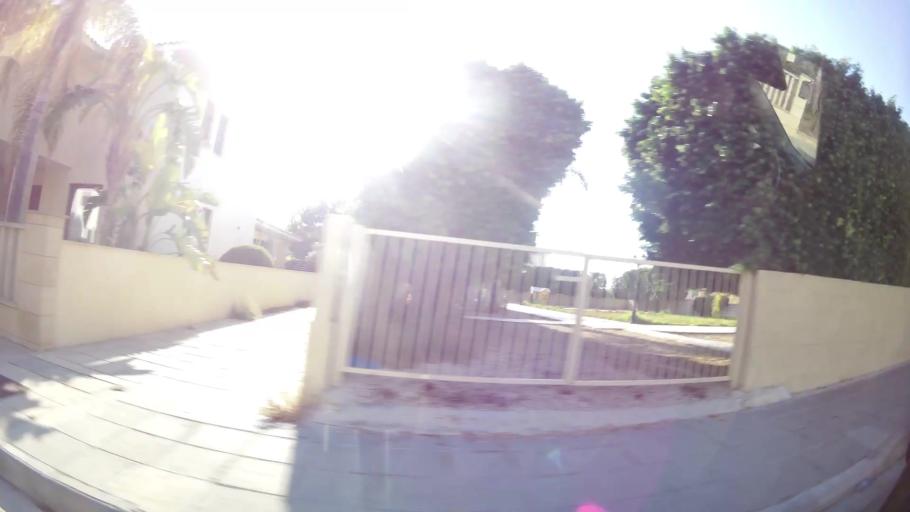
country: CY
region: Larnaka
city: Aradippou
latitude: 34.9389
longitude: 33.5997
